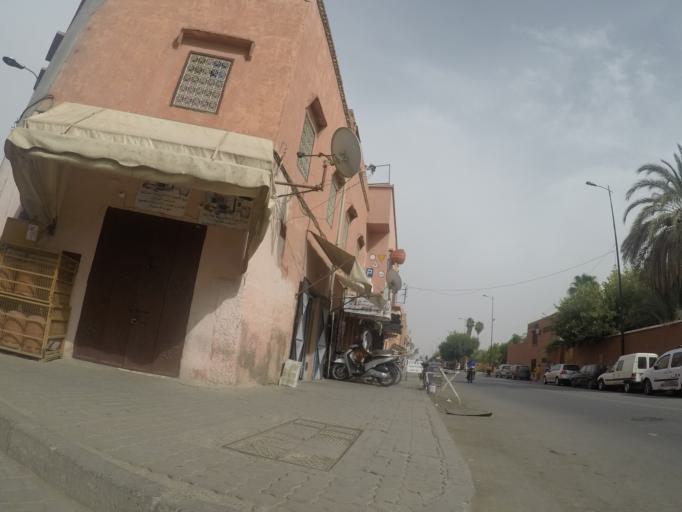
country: MA
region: Marrakech-Tensift-Al Haouz
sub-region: Marrakech
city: Marrakesh
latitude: 31.6182
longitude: -7.9756
